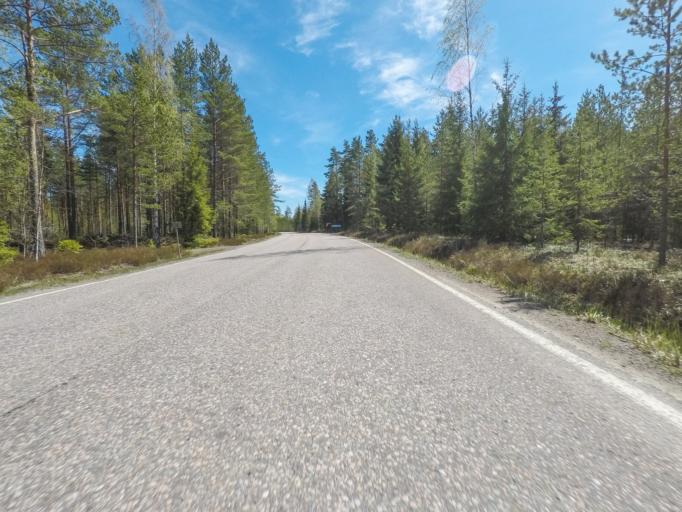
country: FI
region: Uusimaa
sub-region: Helsinki
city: Kaerkoelae
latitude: 60.4924
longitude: 23.8781
